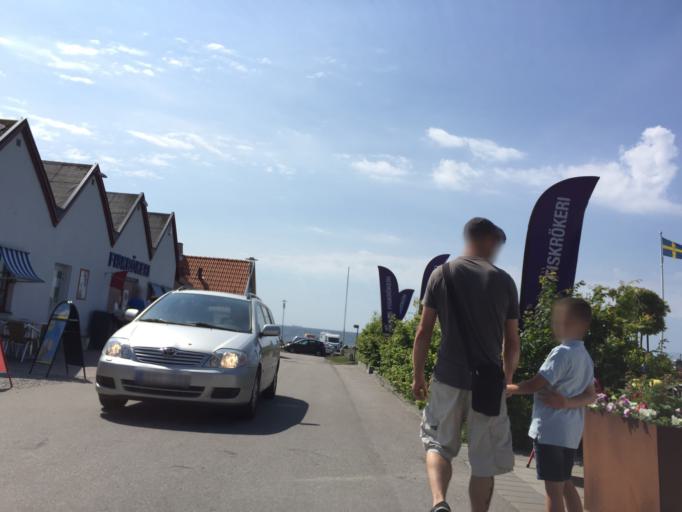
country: SE
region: Skane
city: Smygehamn
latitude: 55.3382
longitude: 13.3596
